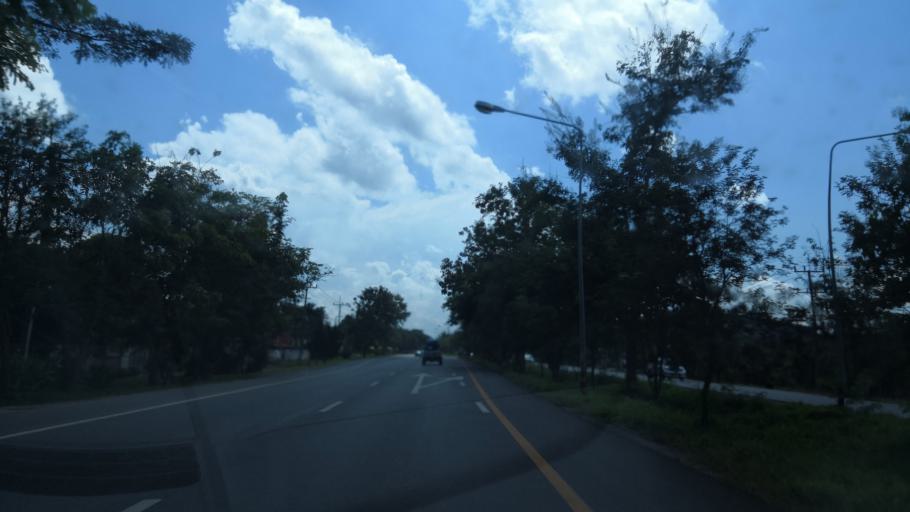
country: TH
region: Chiang Rai
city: Mae Lao
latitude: 19.7714
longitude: 99.7381
